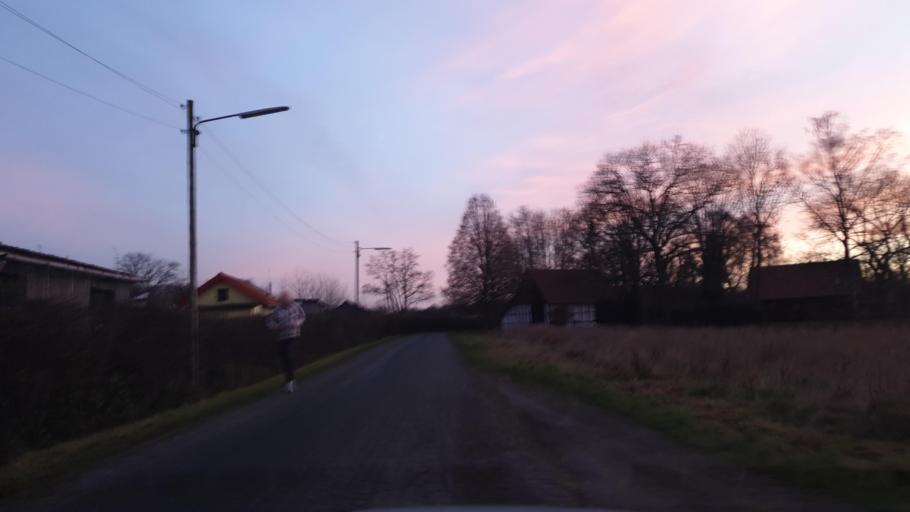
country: DE
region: Lower Saxony
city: Osnabrueck
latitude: 52.2592
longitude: 8.0317
